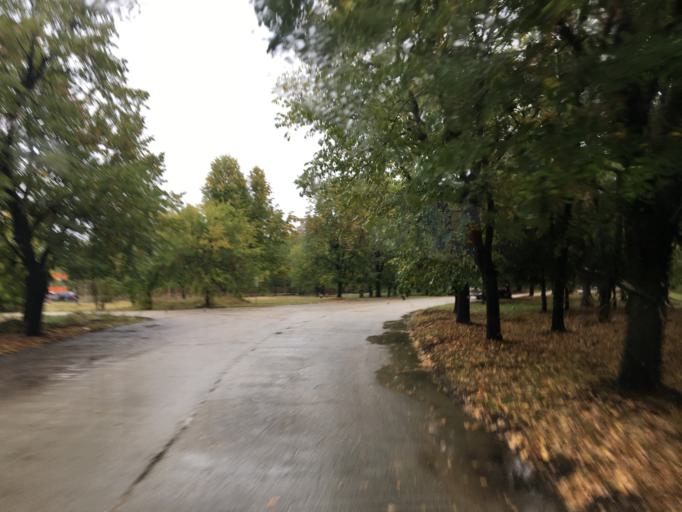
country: BG
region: Lovech
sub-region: Obshtina Lovech
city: Lovech
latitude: 43.1593
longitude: 24.7140
